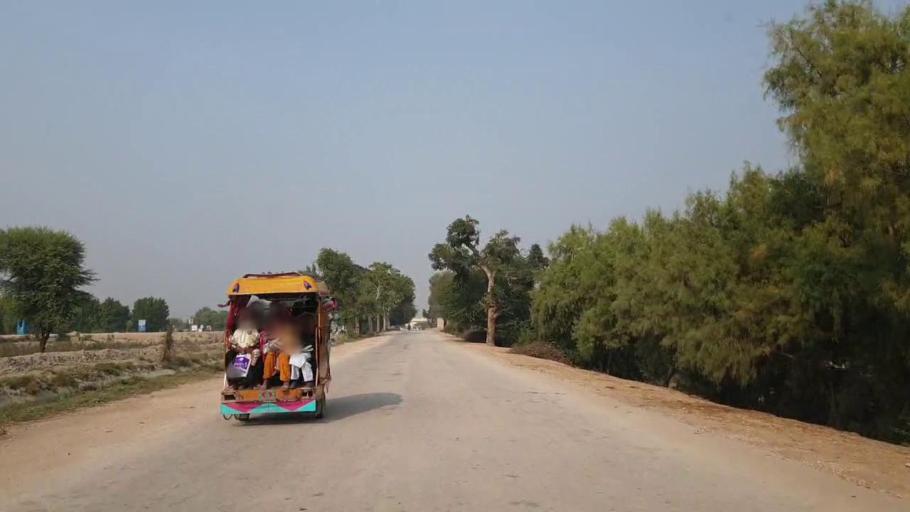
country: PK
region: Sindh
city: Bhan
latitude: 26.5855
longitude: 67.7291
